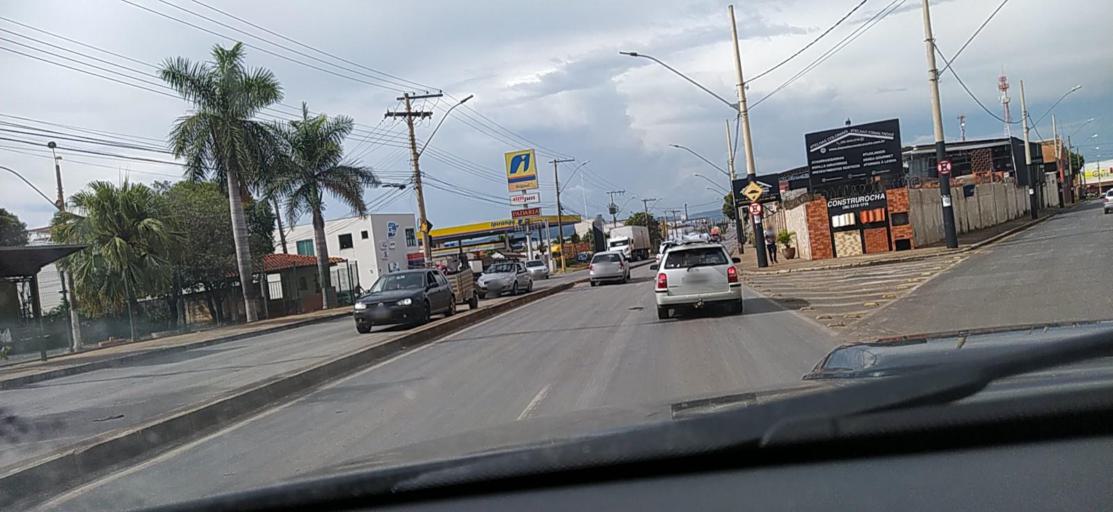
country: BR
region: Minas Gerais
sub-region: Montes Claros
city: Montes Claros
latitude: -16.7333
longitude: -43.8462
